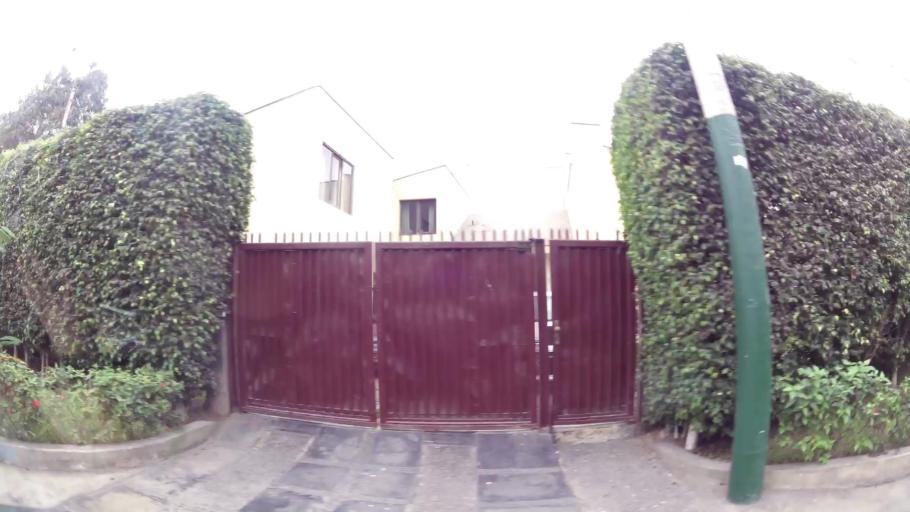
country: PE
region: Lima
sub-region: Lima
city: La Molina
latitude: -12.1084
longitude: -76.9634
